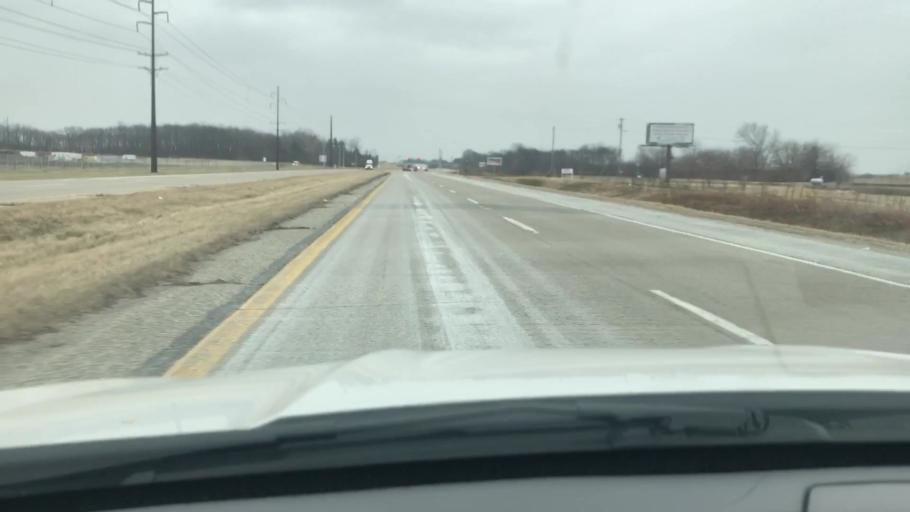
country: US
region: Indiana
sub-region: Tippecanoe County
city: Dayton
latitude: 40.3743
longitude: -86.7969
